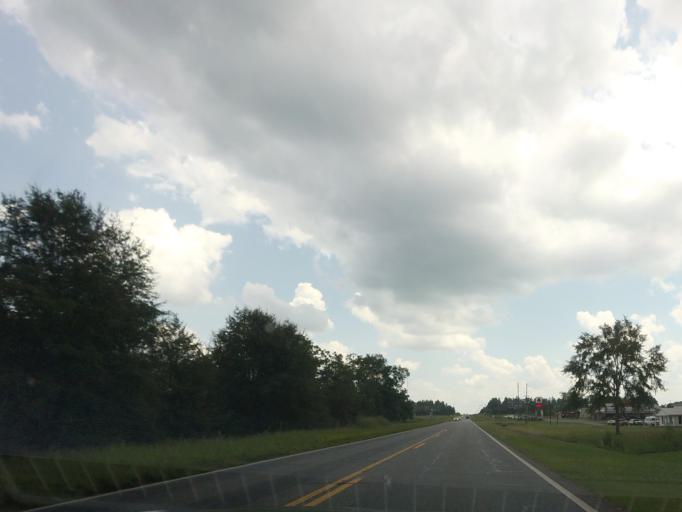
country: US
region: Georgia
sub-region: Bleckley County
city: Cochran
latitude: 32.4121
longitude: -83.3477
